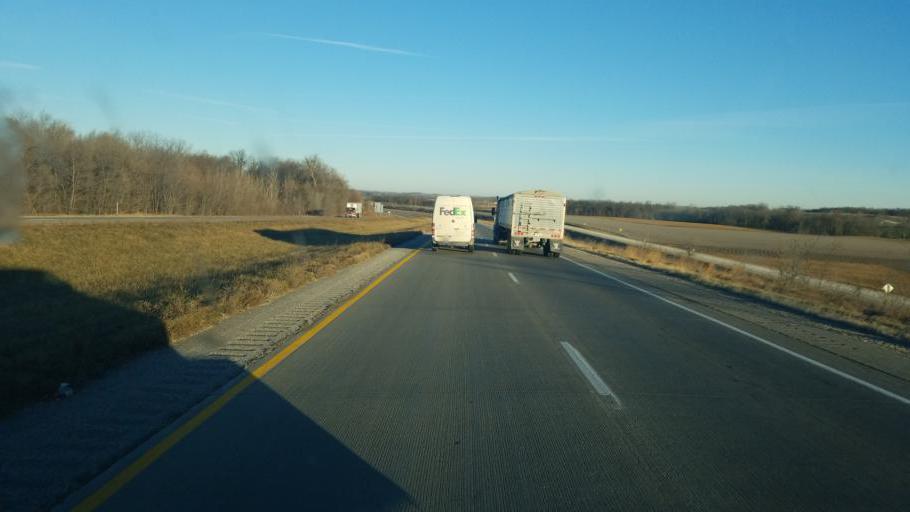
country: US
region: Iowa
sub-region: Wapello County
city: Eddyville
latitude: 41.1627
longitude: -92.6228
